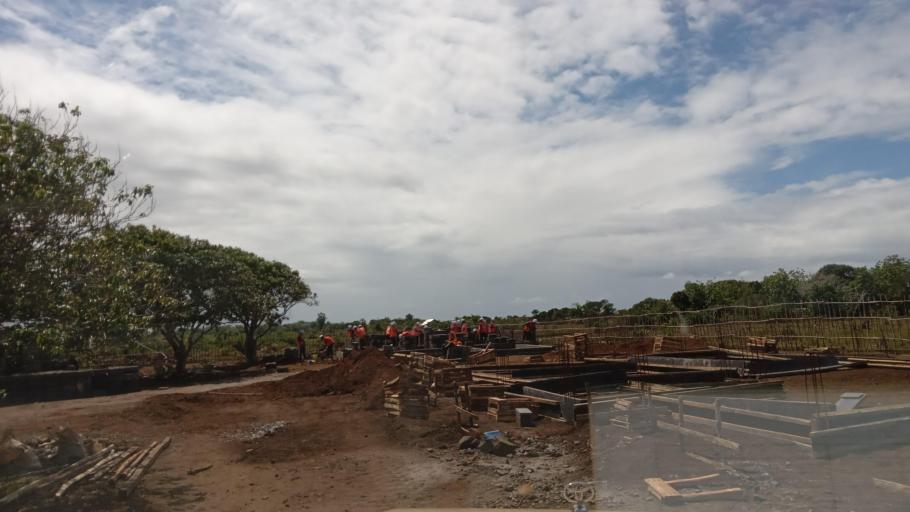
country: MG
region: Atsimo-Atsinanana
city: Vohipaho
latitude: -23.8329
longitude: 47.5539
